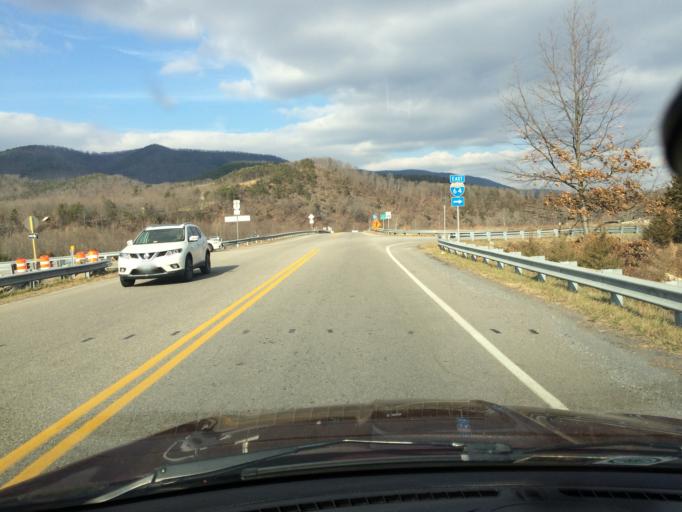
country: US
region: Virginia
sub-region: Alleghany County
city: Clifton Forge
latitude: 37.7908
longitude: -79.8857
